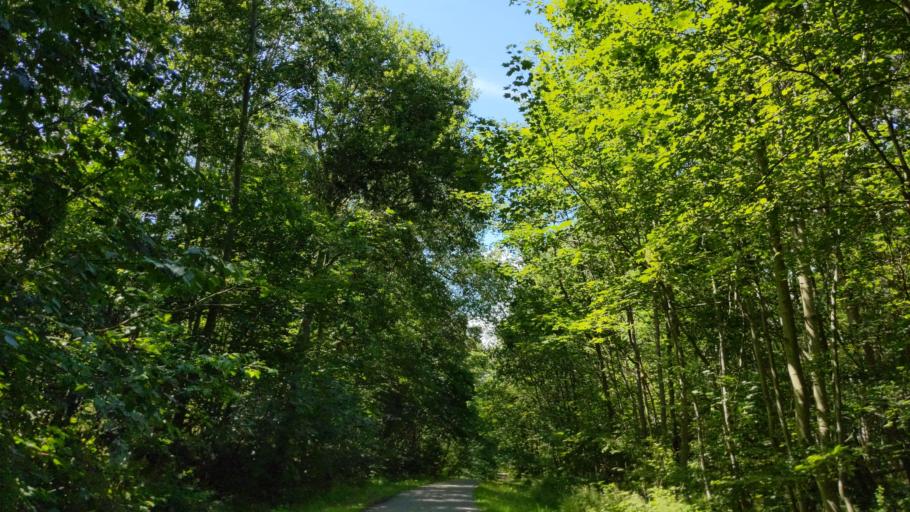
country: DE
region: Mecklenburg-Vorpommern
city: Kalkhorst
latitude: 54.0121
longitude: 11.0984
